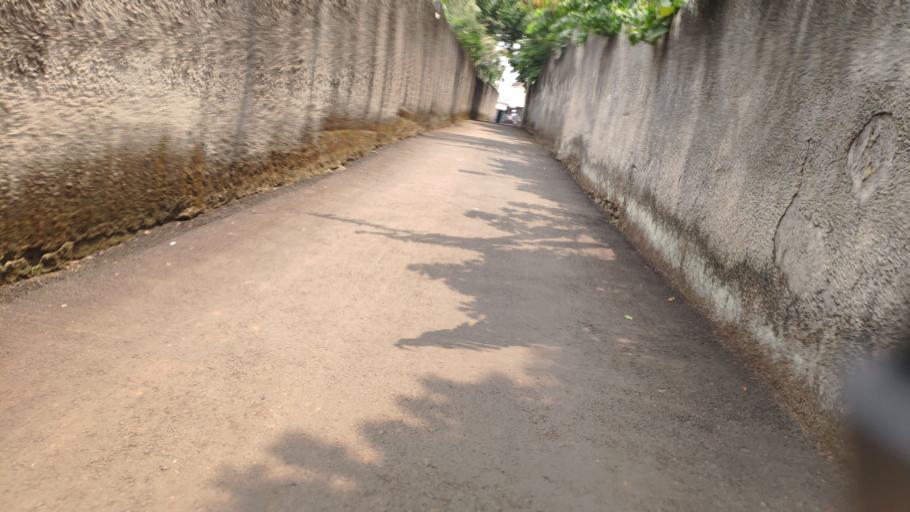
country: ID
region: West Java
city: Depok
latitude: -6.3499
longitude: 106.8192
